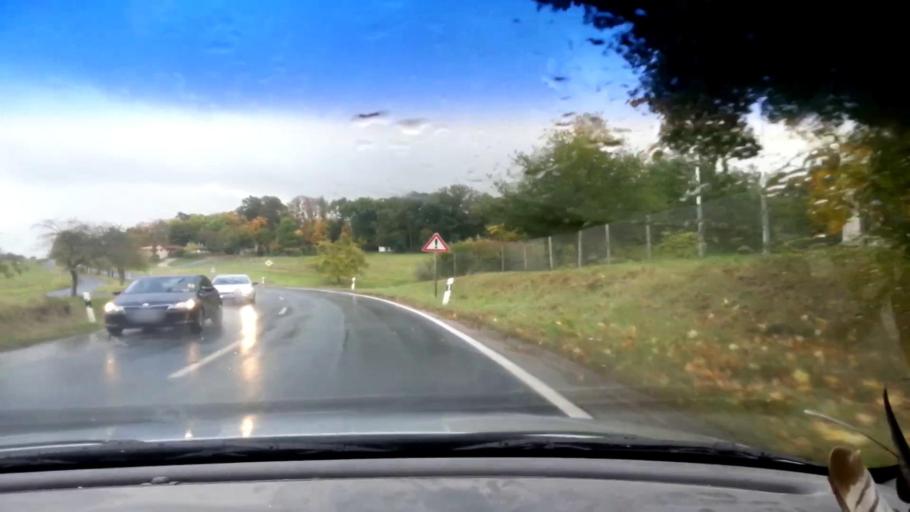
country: DE
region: Bavaria
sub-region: Upper Franconia
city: Burgebrach
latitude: 49.8433
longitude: 10.7315
